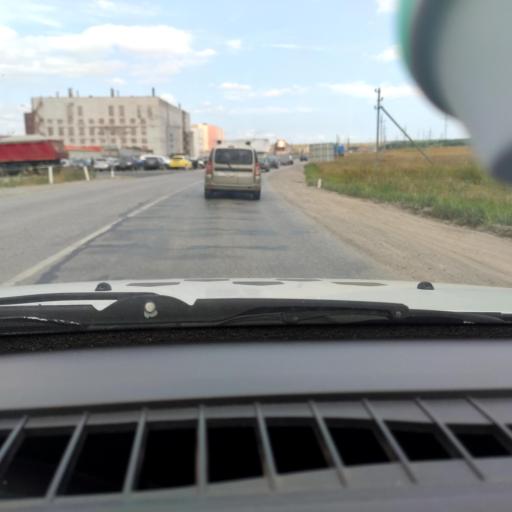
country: RU
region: Perm
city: Solikamsk
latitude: 59.5750
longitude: 56.7674
